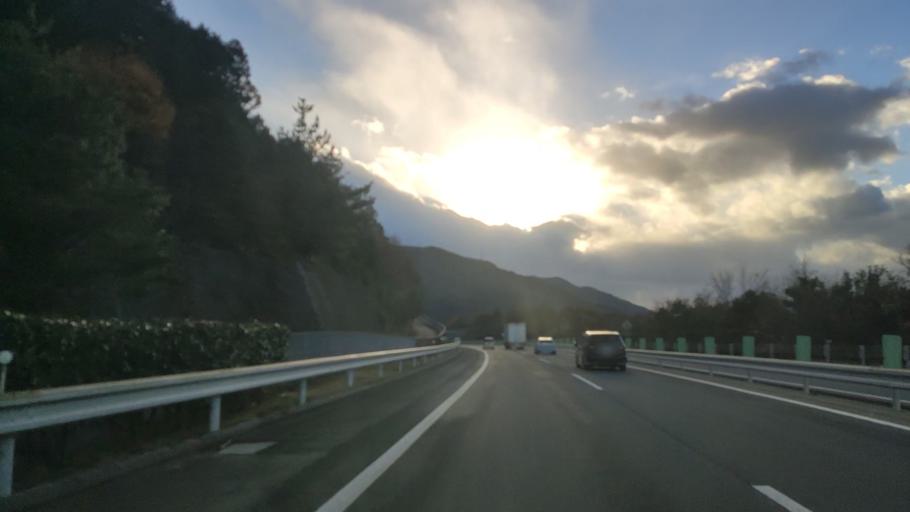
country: JP
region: Ehime
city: Saijo
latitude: 33.8635
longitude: 133.0519
